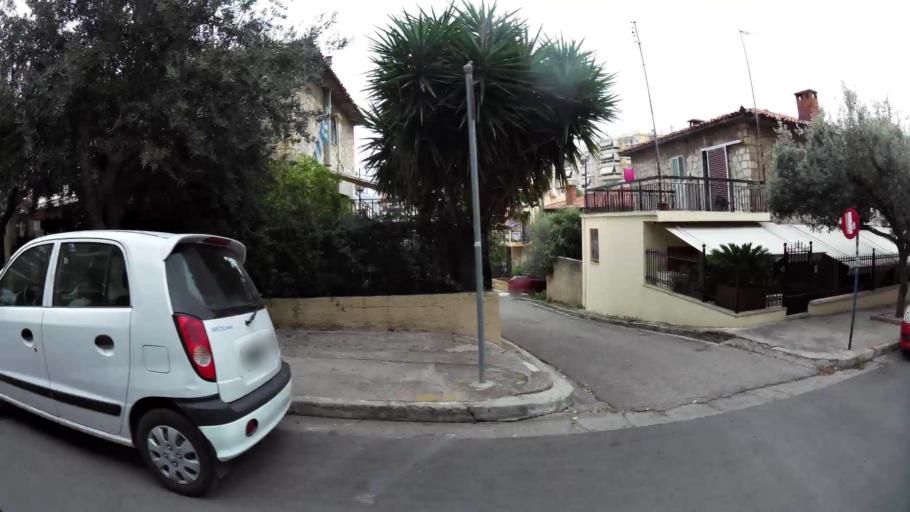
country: GR
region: Attica
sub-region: Nomarchia Athinas
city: Nea Ionia
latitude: 38.0349
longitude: 23.7604
